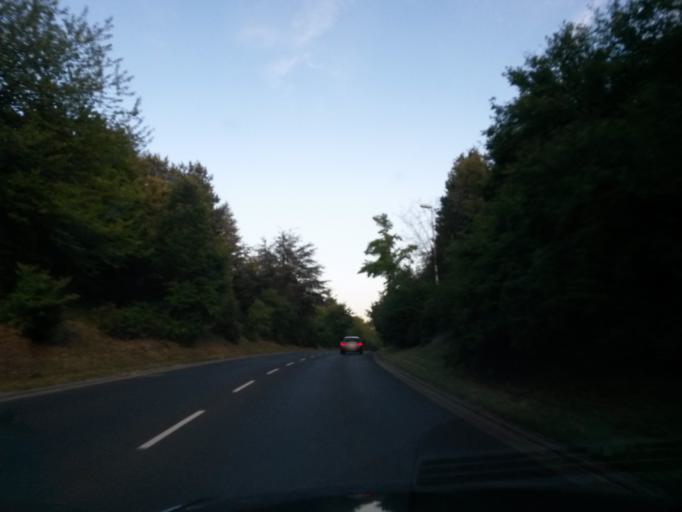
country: DE
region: Bavaria
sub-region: Regierungsbezirk Unterfranken
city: Marktheidenfeld
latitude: 49.8556
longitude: 9.6051
